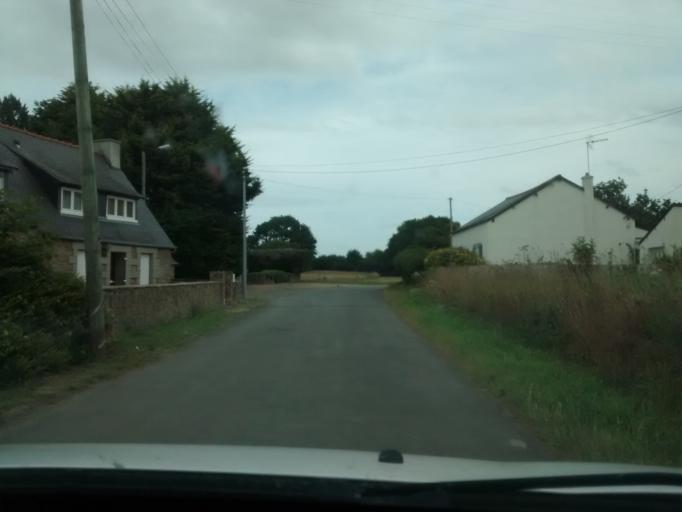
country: FR
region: Brittany
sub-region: Departement des Cotes-d'Armor
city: Penvenan
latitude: 48.8215
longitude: -3.2920
